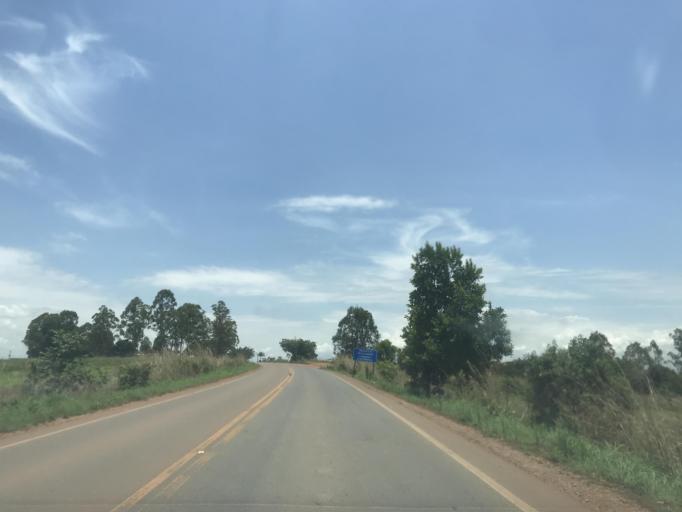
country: BR
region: Goias
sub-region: Vianopolis
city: Vianopolis
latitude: -16.5836
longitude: -48.3451
